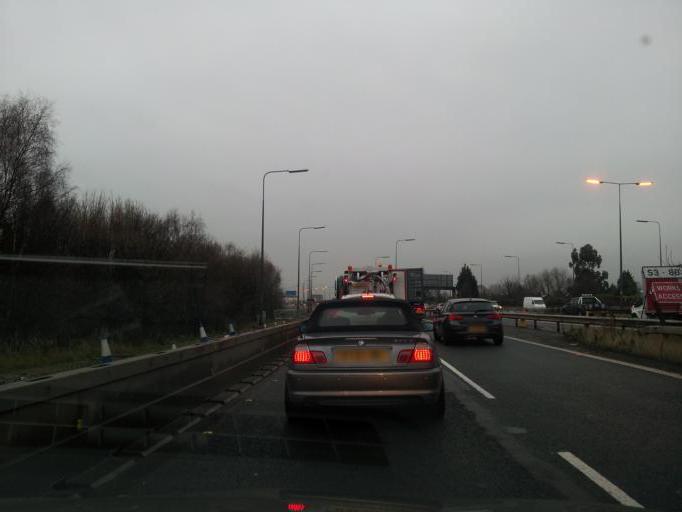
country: GB
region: England
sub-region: Manchester
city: Swinton
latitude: 53.4821
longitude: -2.3757
